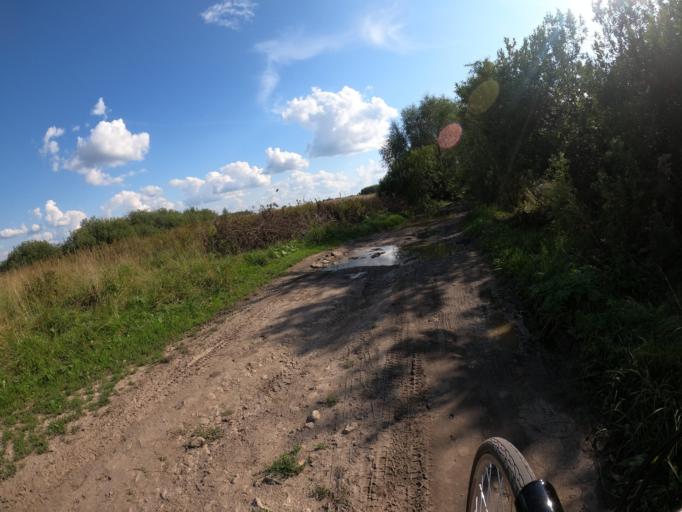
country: RU
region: Moskovskaya
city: Troitskoye
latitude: 55.2312
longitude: 38.4861
